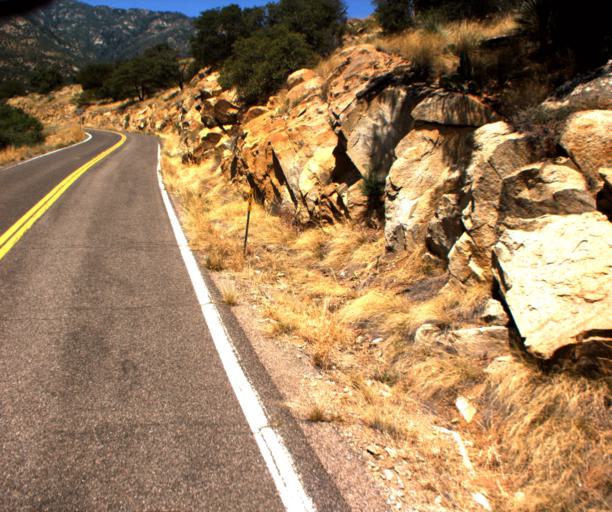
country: US
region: Arizona
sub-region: Graham County
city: Swift Trail Junction
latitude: 32.6699
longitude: -109.7877
